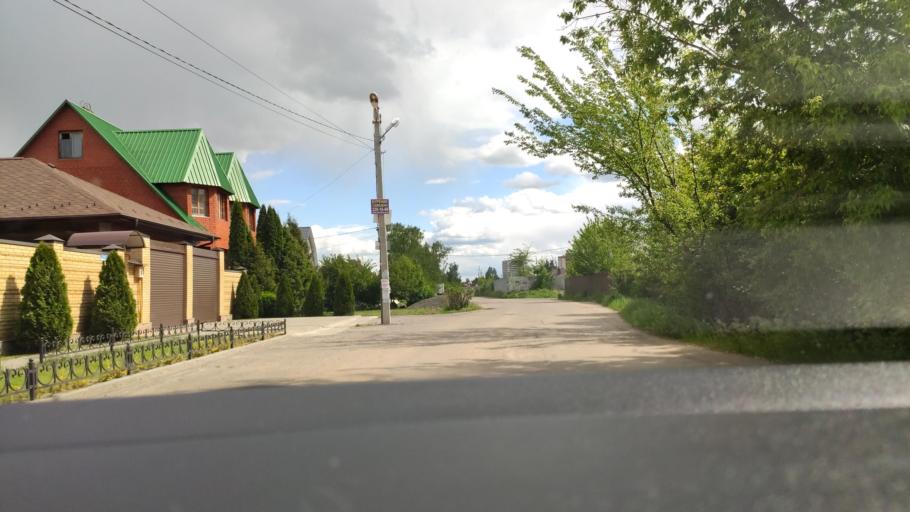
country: RU
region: Voronezj
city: Somovo
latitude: 51.6810
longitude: 39.3168
